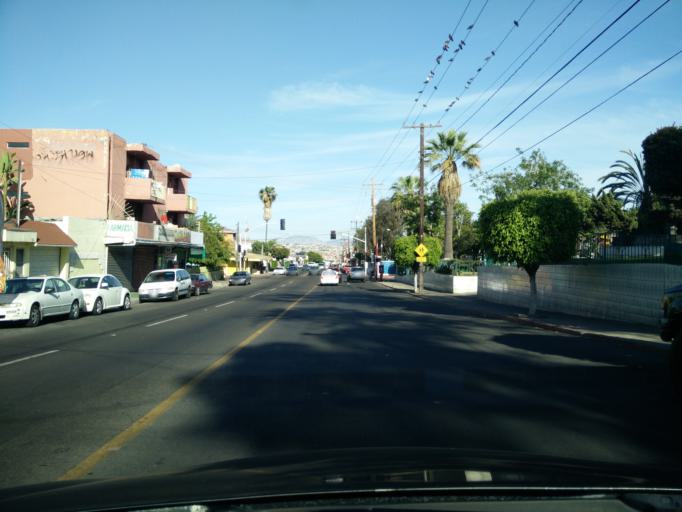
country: MX
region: Baja California
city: Tijuana
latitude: 32.5265
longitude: -117.0440
